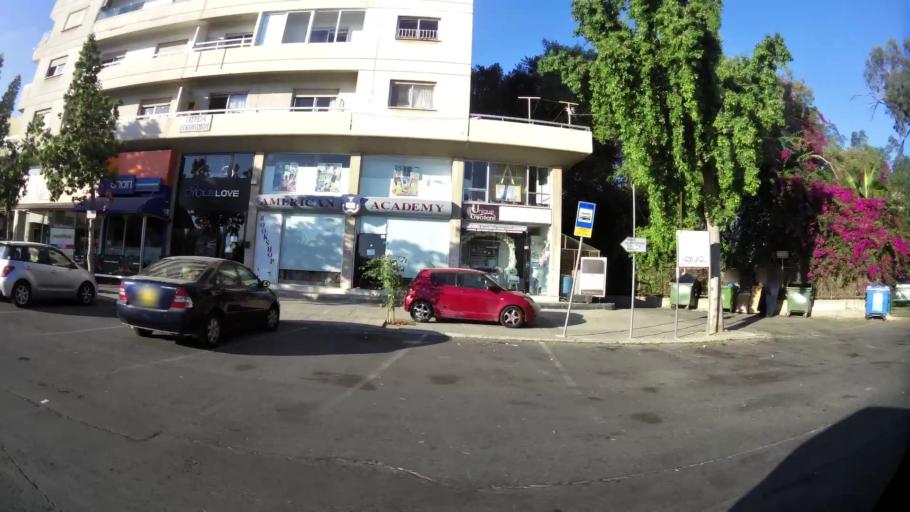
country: CY
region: Larnaka
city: Larnaca
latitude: 34.9177
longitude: 33.6271
